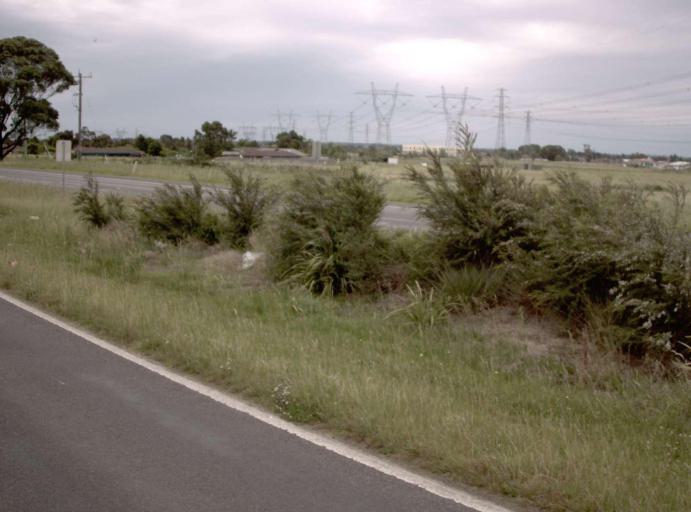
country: AU
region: Victoria
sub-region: Casey
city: Lynbrook
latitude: -38.0648
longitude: 145.2657
